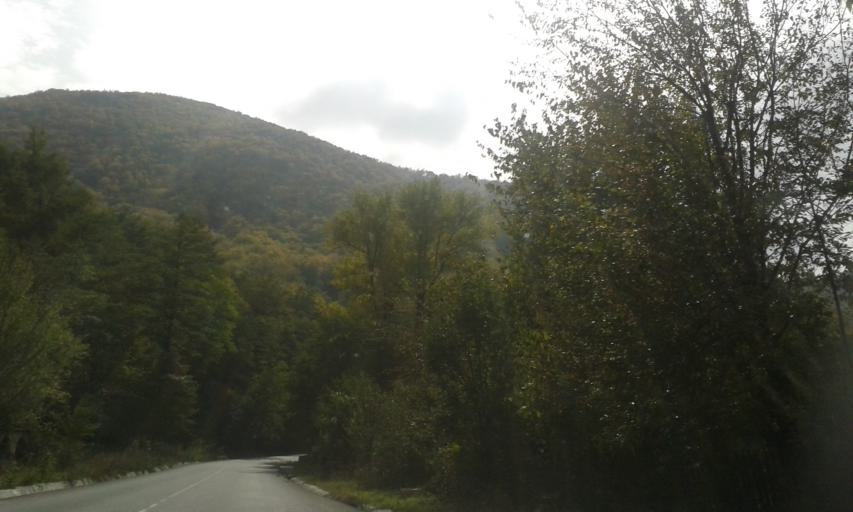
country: RO
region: Gorj
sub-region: Comuna Bumbesti-Jiu
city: Bumbesti-Jiu
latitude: 45.2143
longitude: 23.3807
